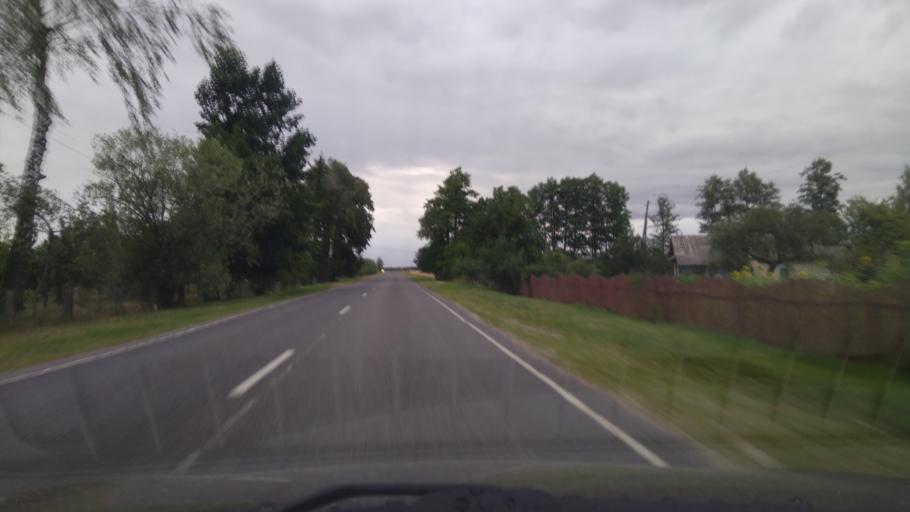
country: BY
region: Brest
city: Byaroza
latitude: 52.4259
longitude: 24.9810
